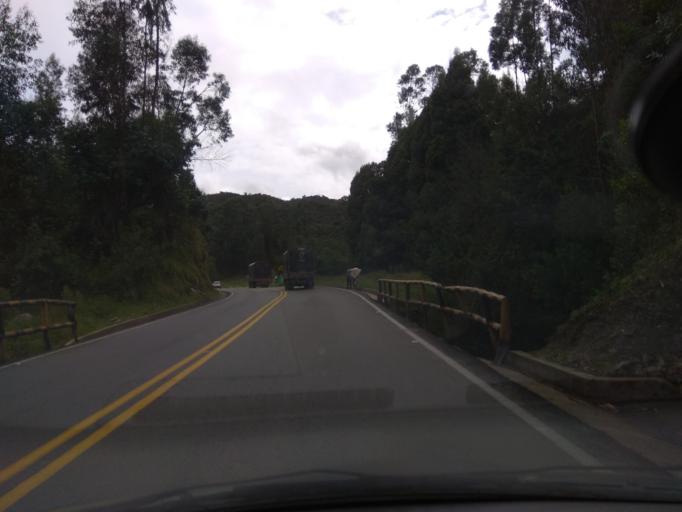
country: CO
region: Boyaca
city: Santa Rosa de Viterbo
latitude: 5.8633
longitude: -73.0096
